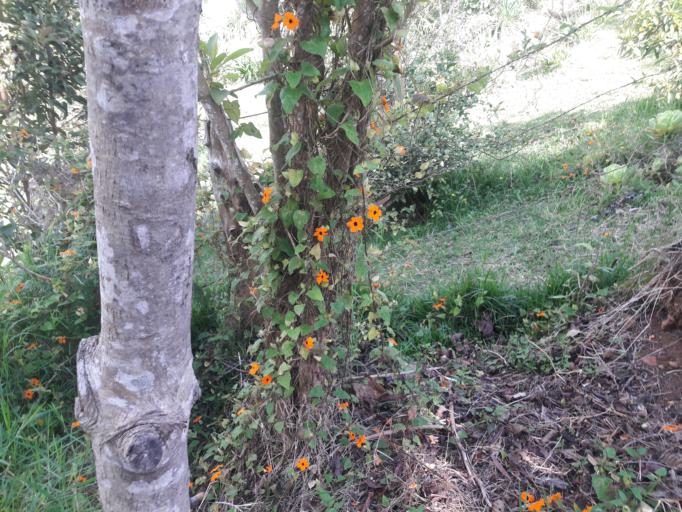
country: CO
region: Valle del Cauca
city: Cali
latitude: 3.4579
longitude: -76.6584
